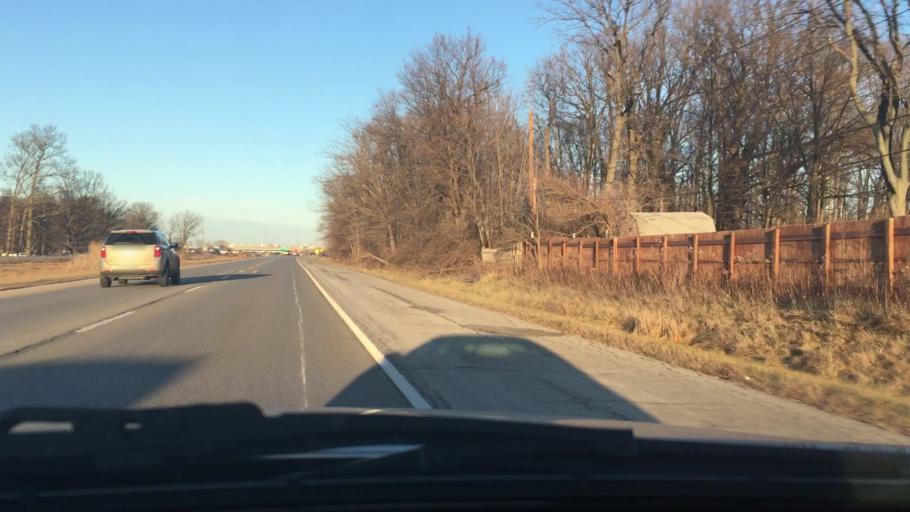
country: US
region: Indiana
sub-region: Marion County
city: Lawrence
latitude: 39.8868
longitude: -86.0629
